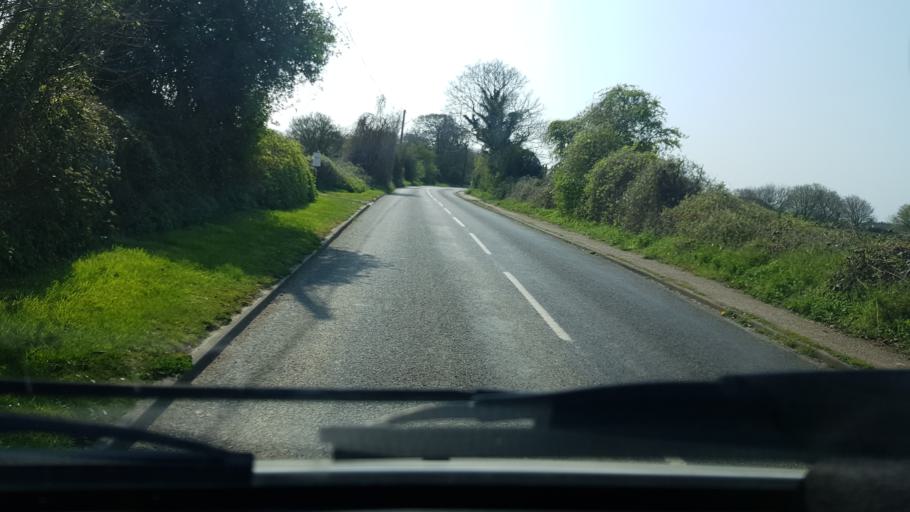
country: GB
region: England
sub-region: West Sussex
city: Chichester
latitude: 50.8306
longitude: -0.8031
